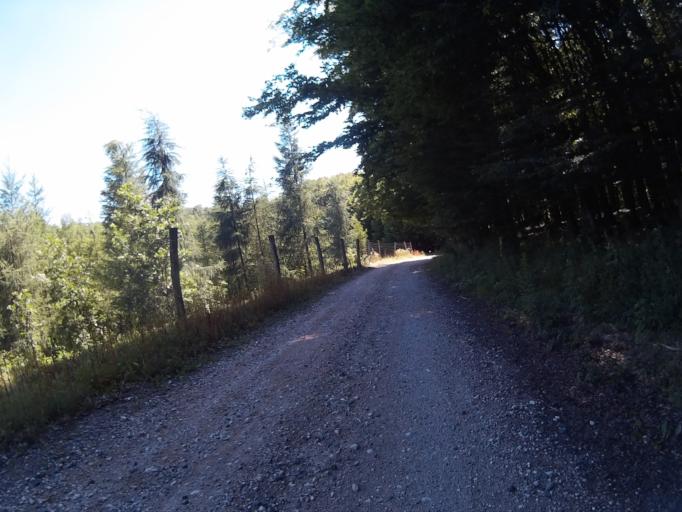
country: HU
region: Veszprem
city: Urkut
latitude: 47.1057
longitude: 17.6708
